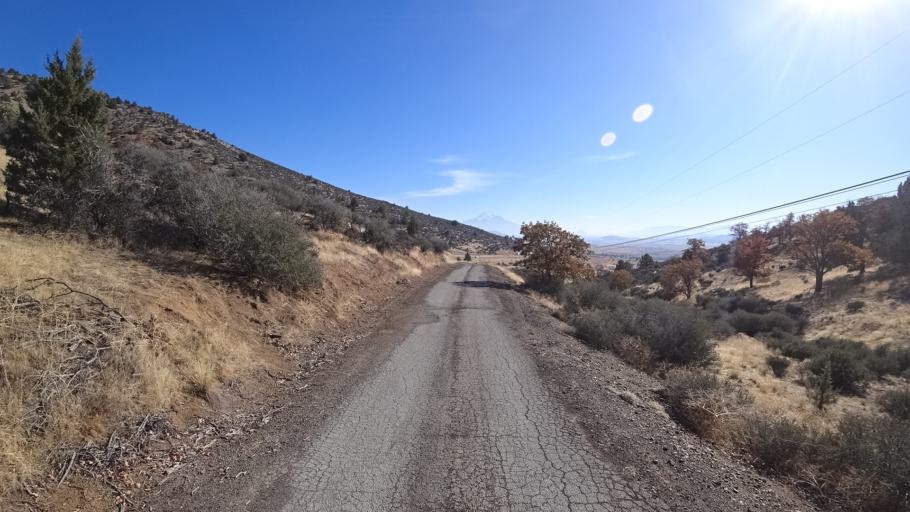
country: US
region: California
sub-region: Siskiyou County
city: Yreka
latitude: 41.7870
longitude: -122.5872
